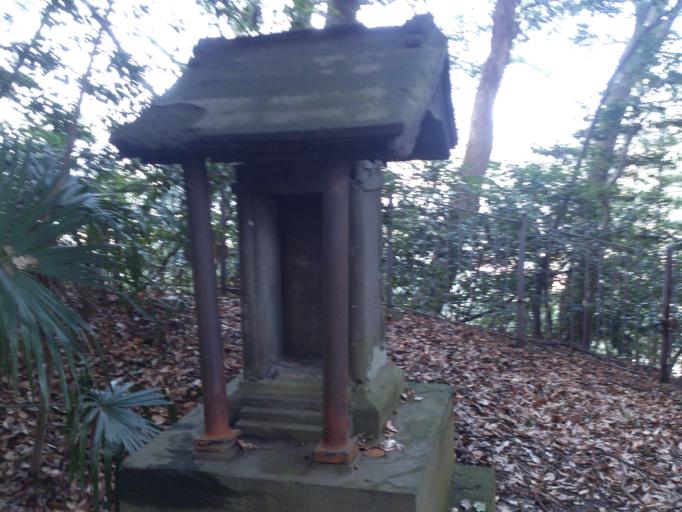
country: JP
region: Chiba
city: Matsudo
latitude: 35.7739
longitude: 139.8978
